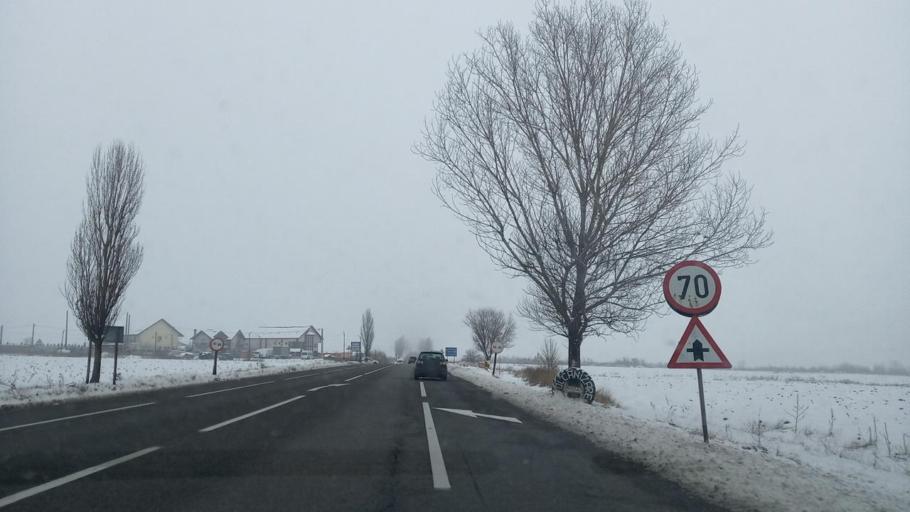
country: RO
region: Bacau
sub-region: Comuna Faraoani
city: Faraoani
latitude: 46.4357
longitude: 26.9230
